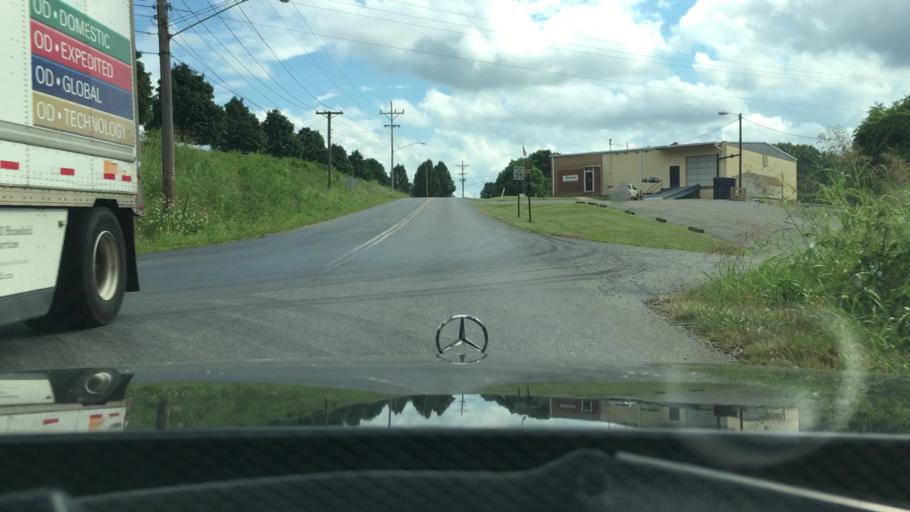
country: US
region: Virginia
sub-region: City of Lynchburg
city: West Lynchburg
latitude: 37.3737
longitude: -79.1632
